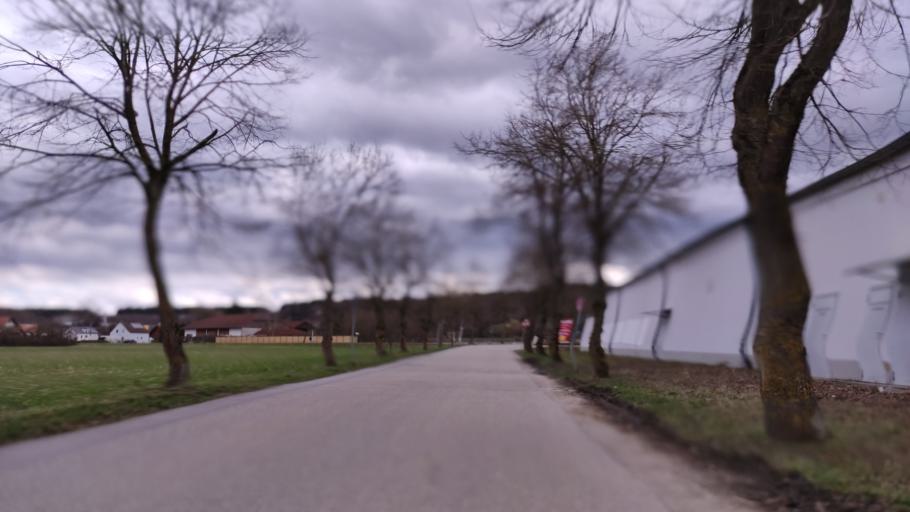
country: DE
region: Bavaria
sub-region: Upper Bavaria
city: Emmering
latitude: 48.1818
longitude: 11.2918
